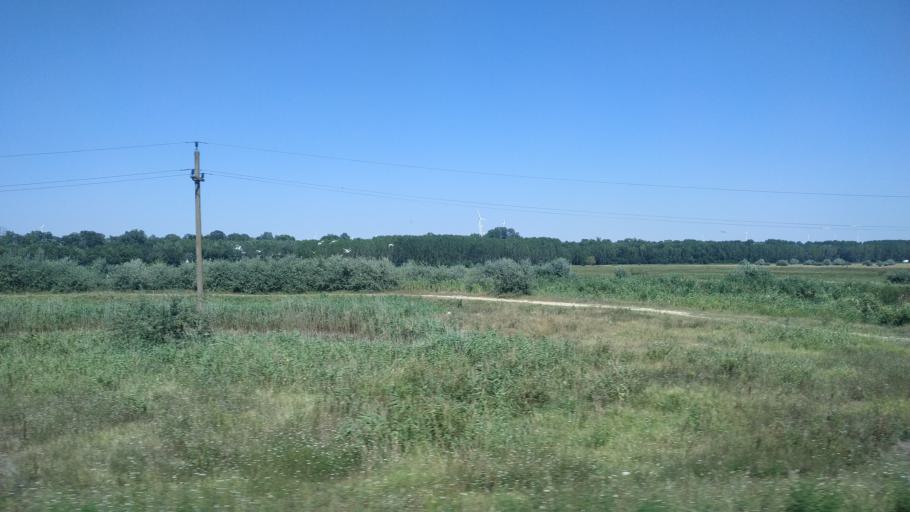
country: RO
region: Constanta
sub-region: Comuna Mircea Voda
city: Mircea Voda
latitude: 44.2649
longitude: 28.1554
